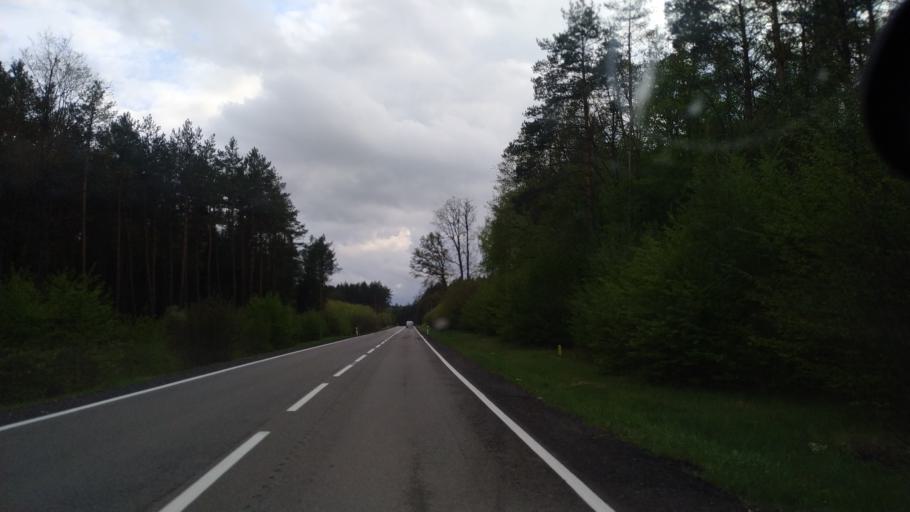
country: PL
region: Pomeranian Voivodeship
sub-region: Powiat kwidzynski
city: Ryjewo
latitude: 53.8247
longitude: 18.9865
